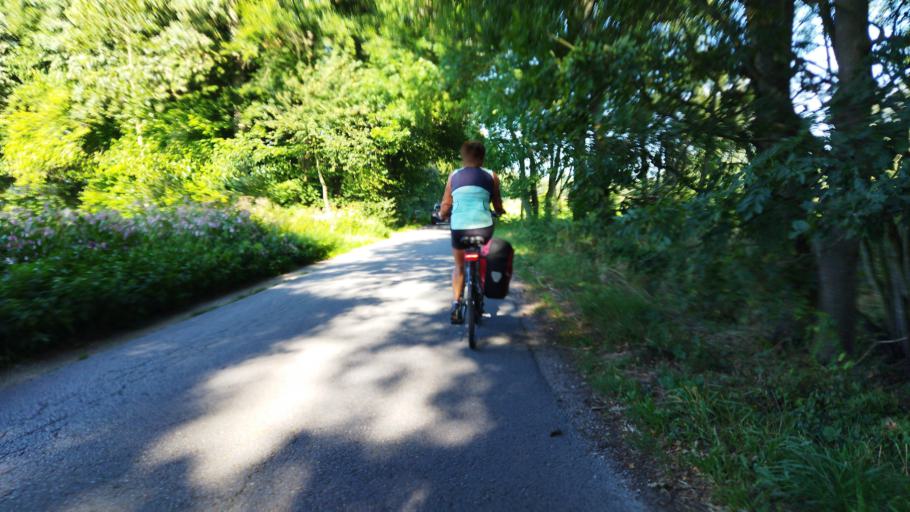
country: DE
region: Lower Saxony
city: Bad Iburg
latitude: 52.1192
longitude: 8.0320
